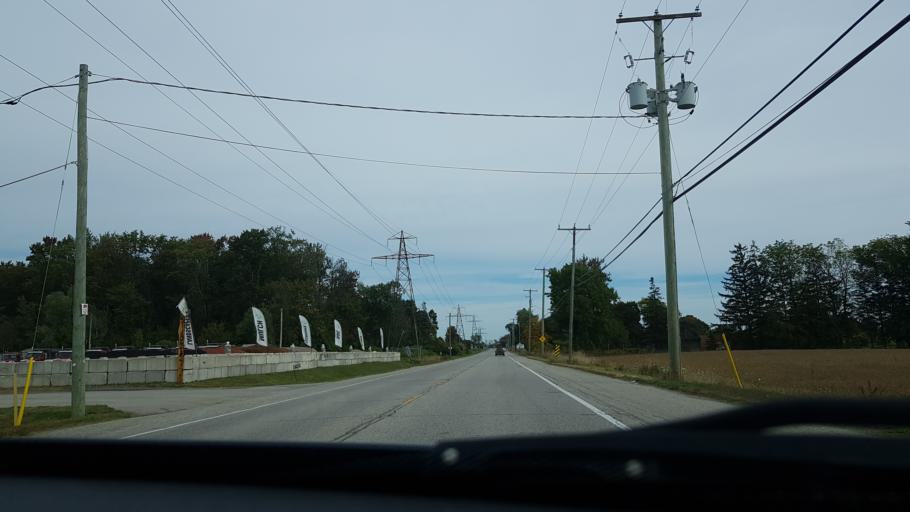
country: CA
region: Ontario
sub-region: Wellington County
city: Guelph
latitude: 43.5002
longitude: -80.2730
